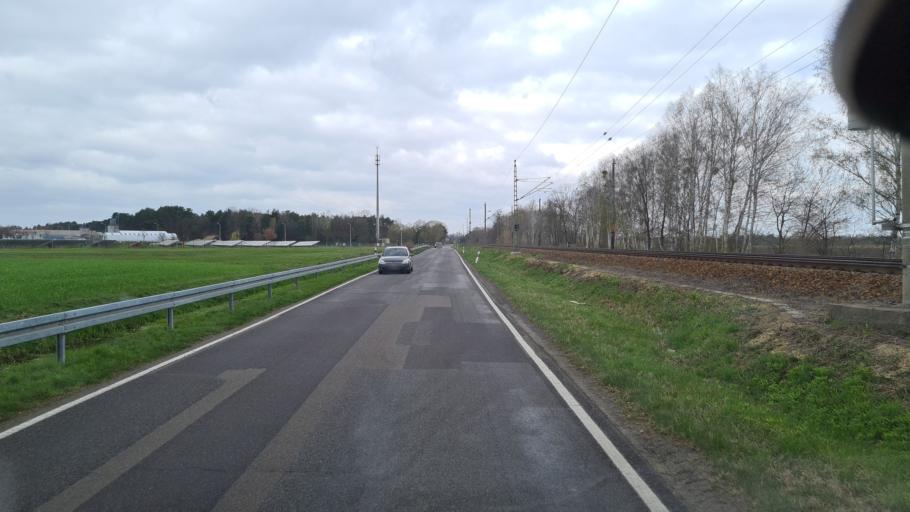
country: DE
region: Brandenburg
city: Ruhland
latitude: 51.4573
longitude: 13.8938
